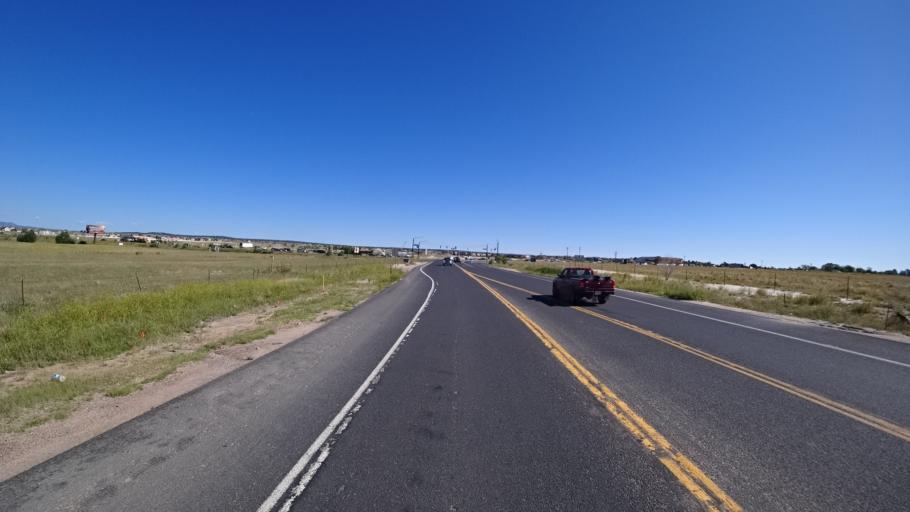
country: US
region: Colorado
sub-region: El Paso County
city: Black Forest
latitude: 38.9391
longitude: -104.6784
